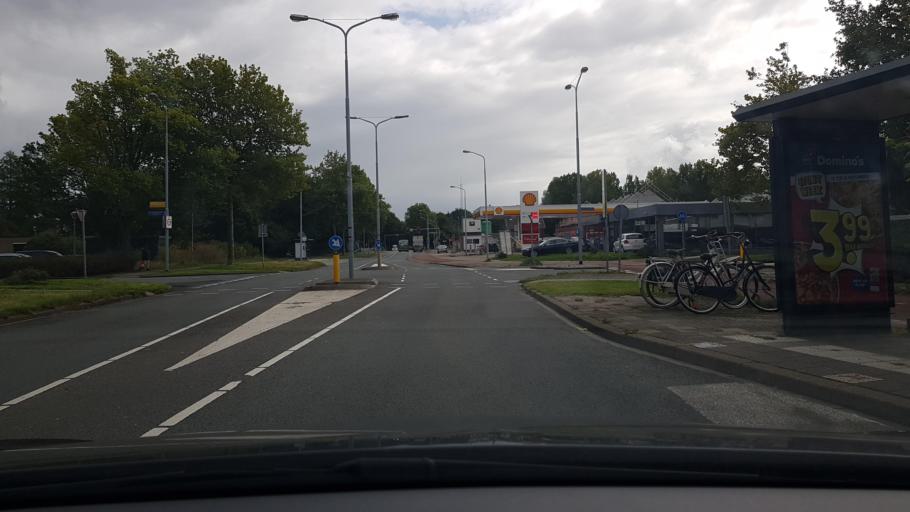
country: NL
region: South Holland
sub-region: Gemeente Hillegom
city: Hillegom
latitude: 52.2620
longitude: 4.6257
